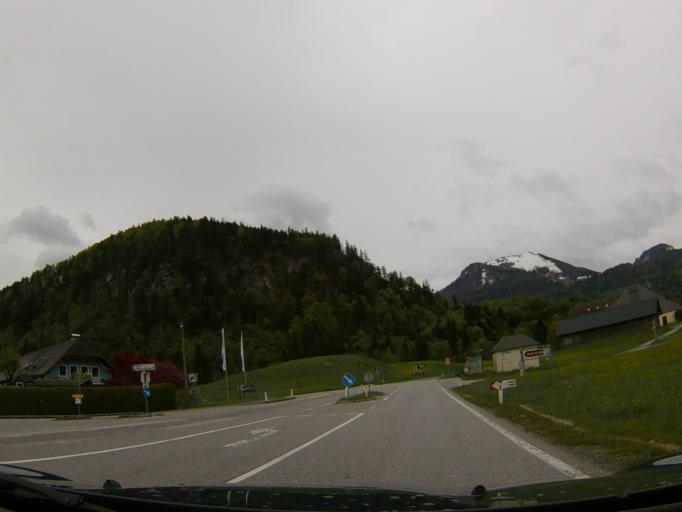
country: AT
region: Salzburg
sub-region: Politischer Bezirk Salzburg-Umgebung
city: Sankt Gilgen
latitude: 47.7765
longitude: 13.3832
